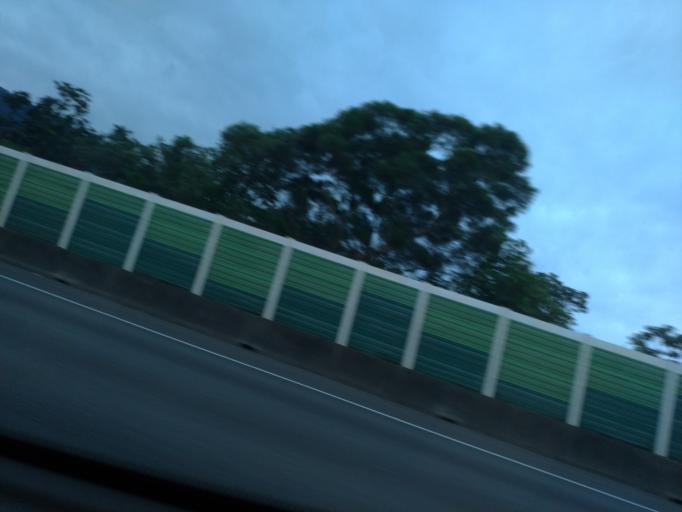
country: TW
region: Taiwan
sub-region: Taoyuan
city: Taoyuan
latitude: 24.9372
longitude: 121.3386
